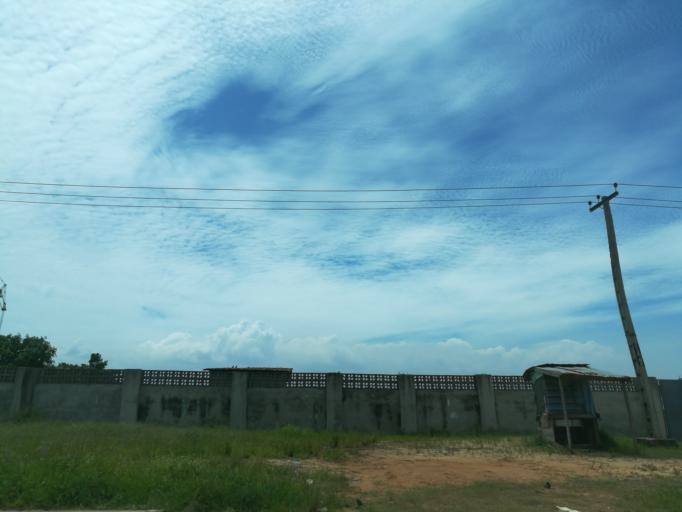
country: NG
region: Lagos
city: Ebute Ikorodu
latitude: 6.5818
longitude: 3.4895
